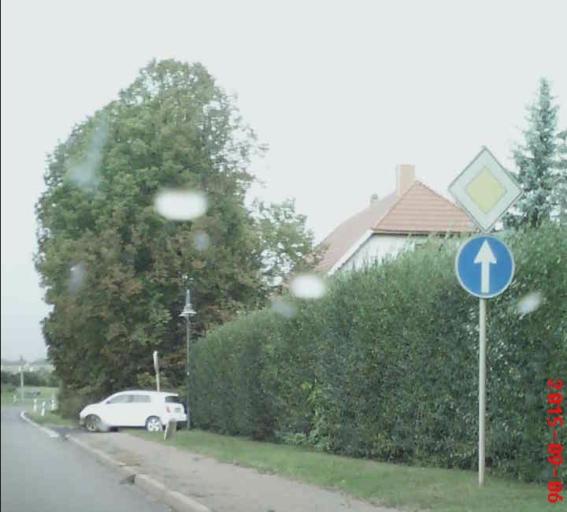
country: DE
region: Thuringia
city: Seebach
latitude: 51.1825
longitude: 10.5008
